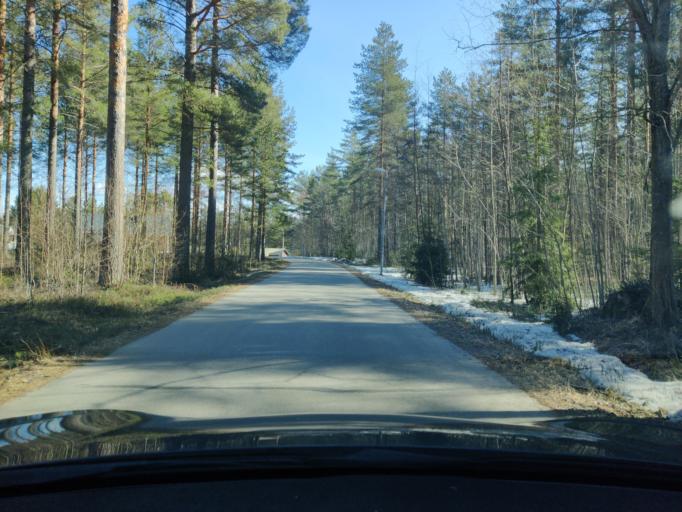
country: FI
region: Northern Savo
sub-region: Kuopio
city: Vehmersalmi
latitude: 62.7695
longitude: 27.9887
